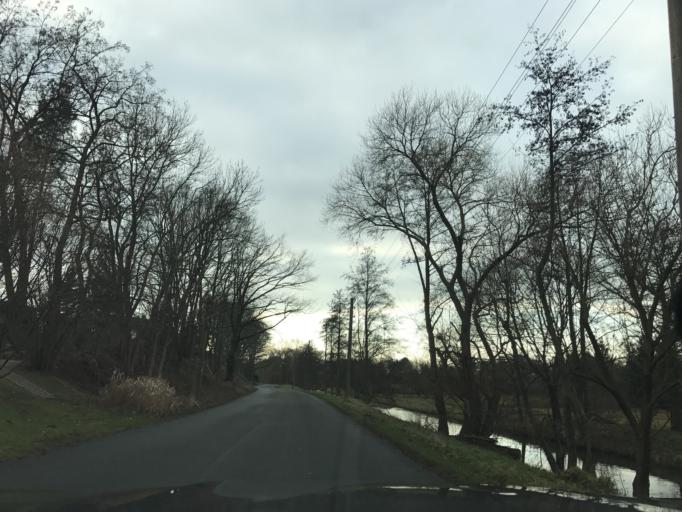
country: DE
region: Brandenburg
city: Brandenburg an der Havel
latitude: 52.3664
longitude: 12.5473
